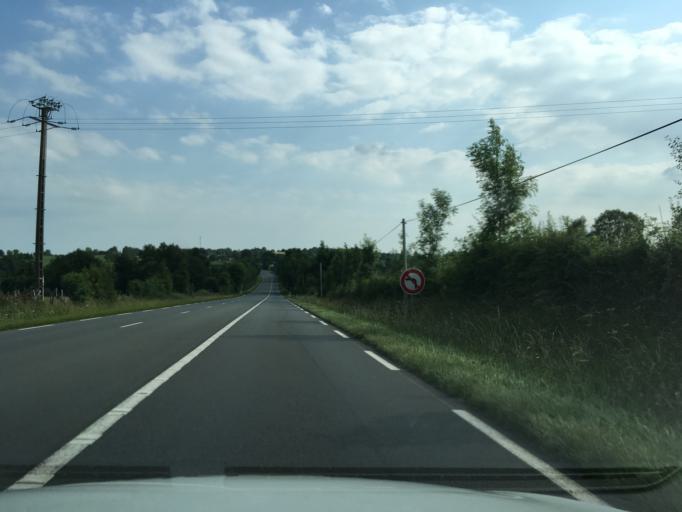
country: FR
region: Poitou-Charentes
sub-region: Departement des Deux-Sevres
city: Saint-Pardoux
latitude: 46.5925
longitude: -0.2908
